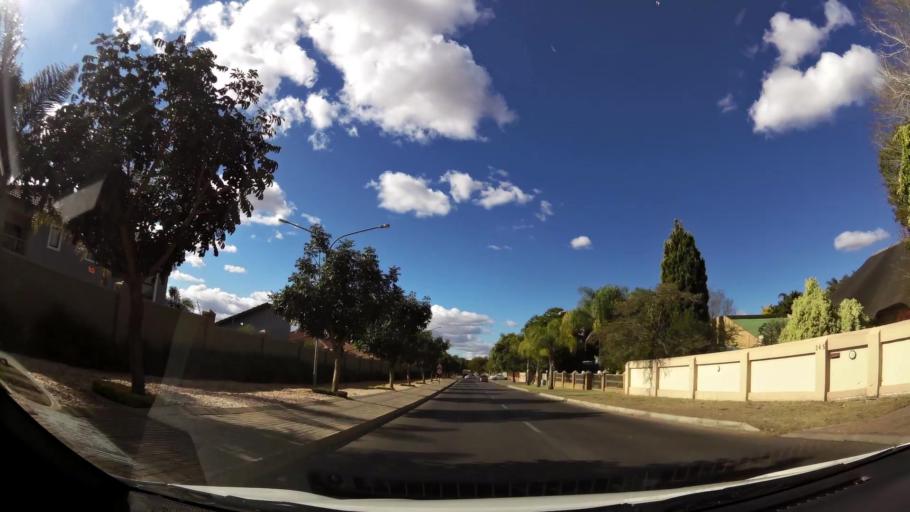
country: ZA
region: Limpopo
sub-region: Capricorn District Municipality
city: Polokwane
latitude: -23.8805
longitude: 29.4903
